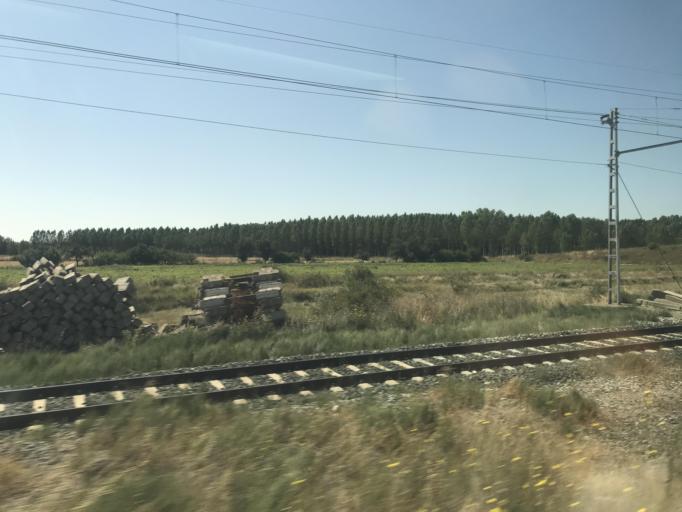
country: ES
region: Castille and Leon
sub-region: Provincia de Burgos
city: Estepar
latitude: 42.2719
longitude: -3.8947
